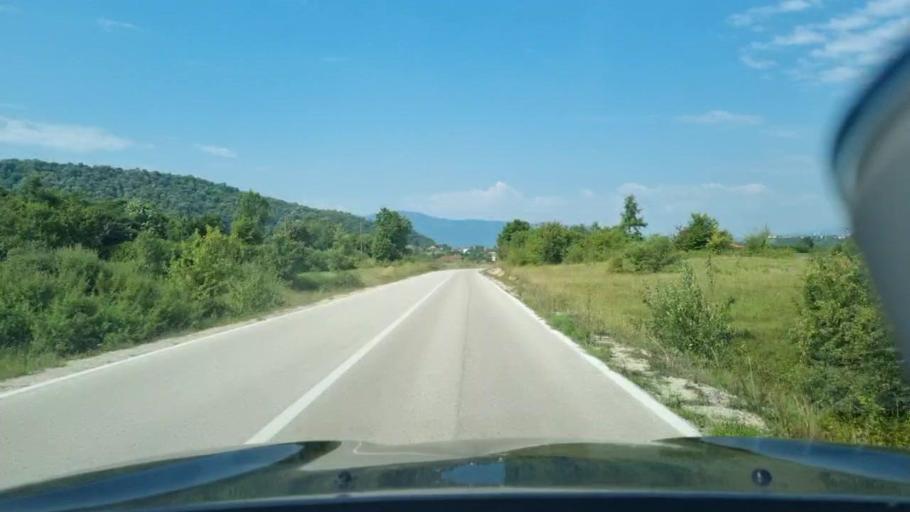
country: BA
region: Federation of Bosnia and Herzegovina
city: Ostrozac
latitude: 44.8835
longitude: 15.9225
